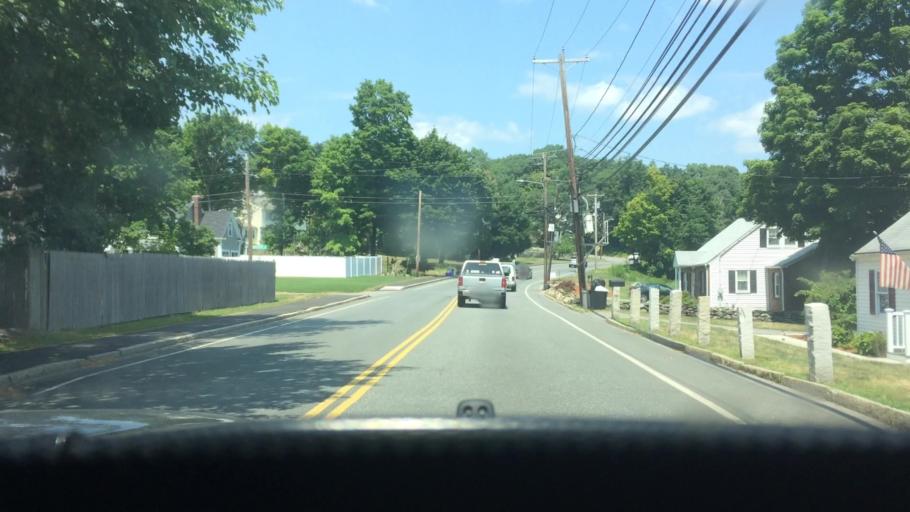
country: US
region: Massachusetts
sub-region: Middlesex County
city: Chelmsford
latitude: 42.6069
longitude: -71.3564
